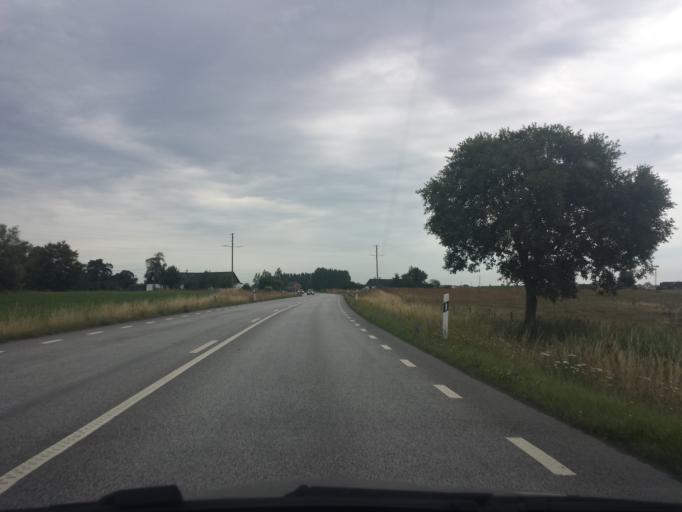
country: SE
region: Skane
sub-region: Ystads Kommun
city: Kopingebro
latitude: 55.4341
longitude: 13.9764
